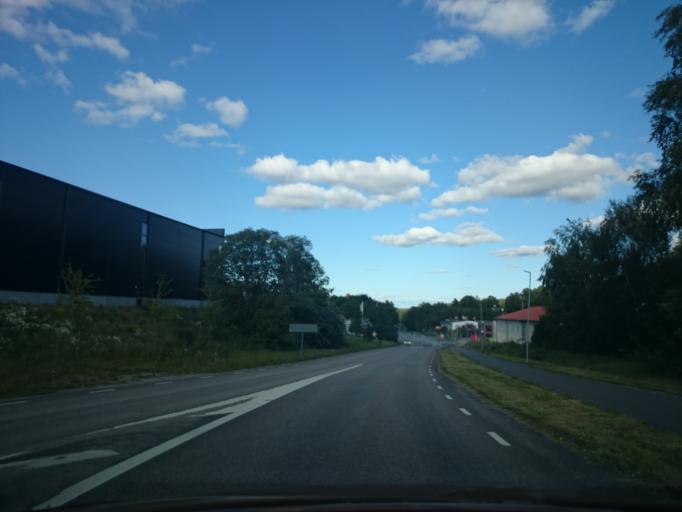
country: SE
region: Vaestra Goetaland
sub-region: Harryda Kommun
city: Molnlycke
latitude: 57.6712
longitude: 12.1318
